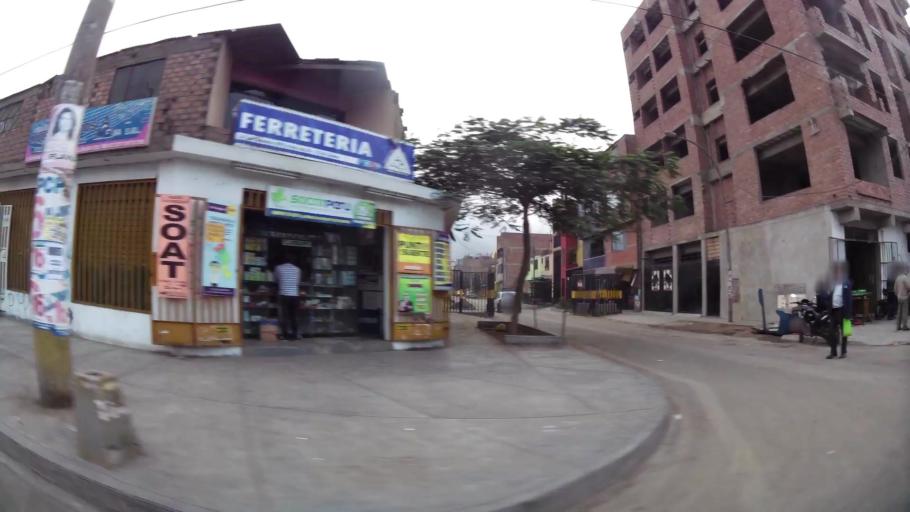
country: PE
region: Lima
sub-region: Lima
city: Independencia
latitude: -11.9976
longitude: -77.0052
